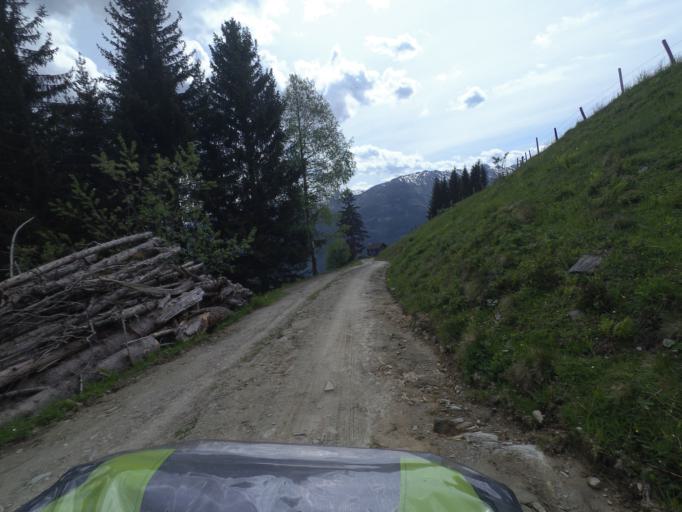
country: AT
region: Salzburg
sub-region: Politischer Bezirk Sankt Johann im Pongau
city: Dorfgastein
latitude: 47.2575
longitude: 13.1234
